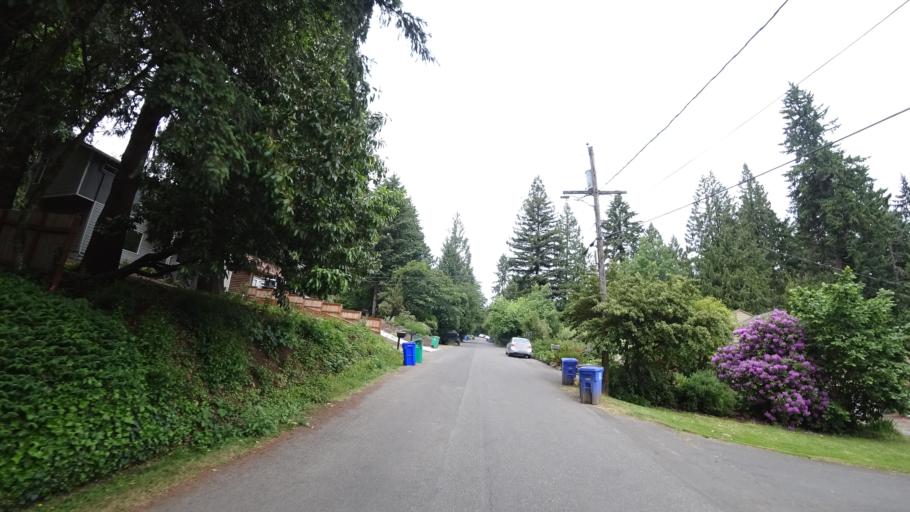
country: US
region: Oregon
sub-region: Clackamas County
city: Lake Oswego
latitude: 45.4564
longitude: -122.6909
